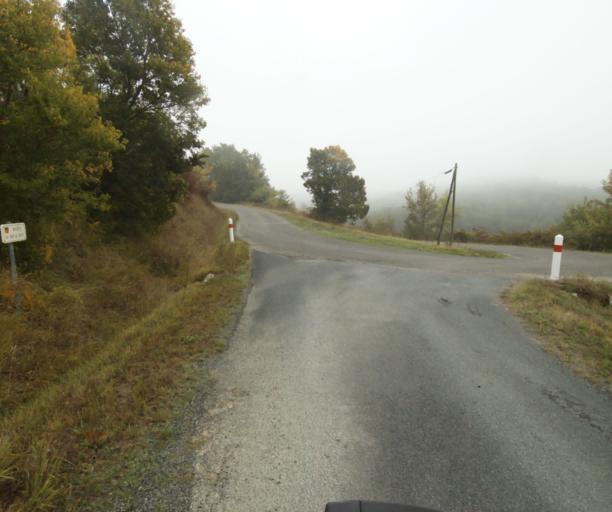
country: FR
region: Midi-Pyrenees
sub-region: Departement de la Haute-Garonne
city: Villemur-sur-Tarn
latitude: 43.8884
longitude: 1.4864
